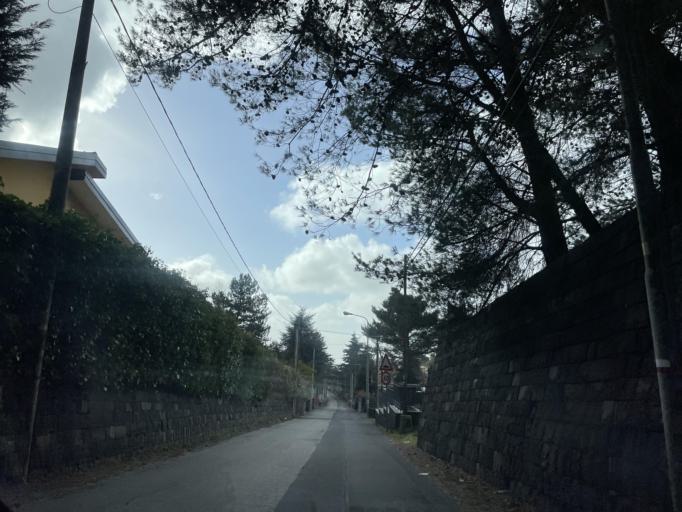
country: IT
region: Sicily
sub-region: Catania
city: Nicolosi
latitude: 37.6232
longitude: 15.0248
